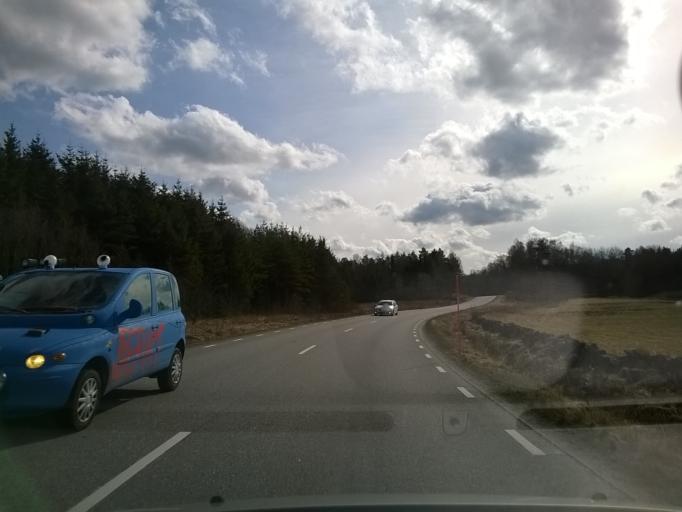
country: SE
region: Vaestra Goetaland
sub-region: Kungalvs Kommun
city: Kode
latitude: 57.9712
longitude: 11.8374
